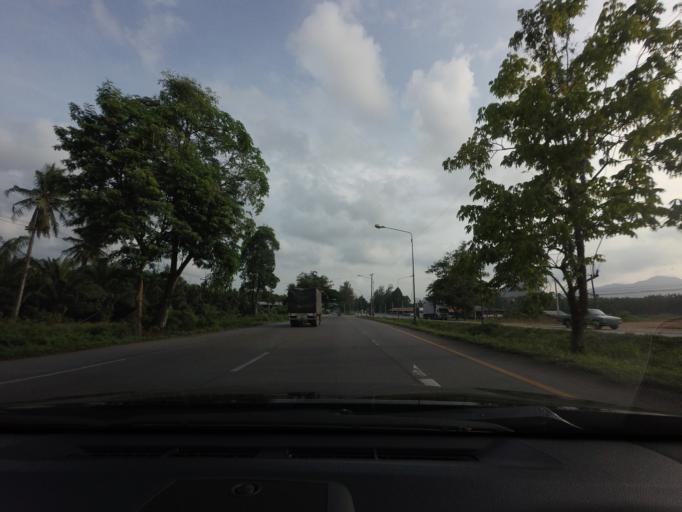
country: TH
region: Chumphon
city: Lamae
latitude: 9.8512
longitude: 99.0564
